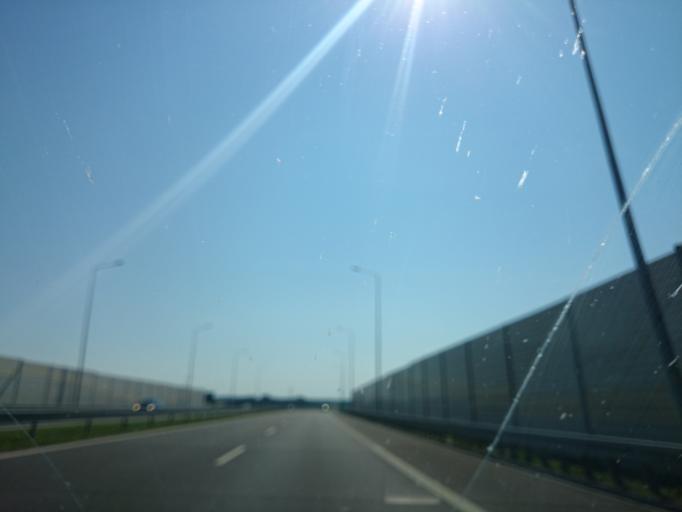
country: PL
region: West Pomeranian Voivodeship
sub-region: Powiat pyrzycki
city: Lipiany
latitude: 52.9489
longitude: 14.9582
